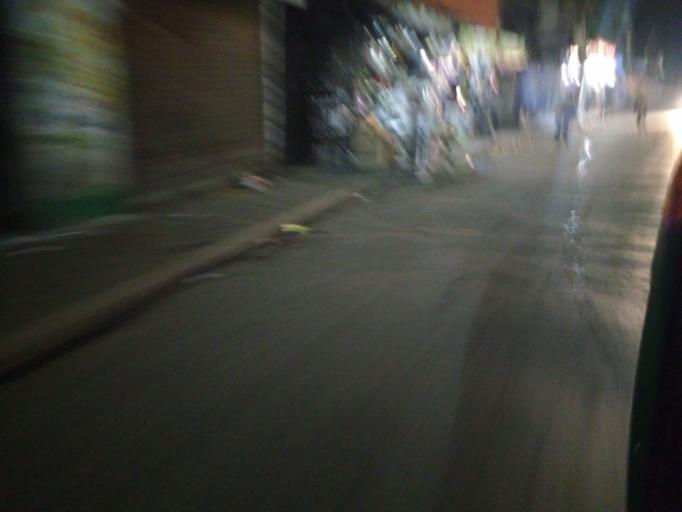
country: IN
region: West Bengal
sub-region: North 24 Parganas
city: Baranagar
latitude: 22.6324
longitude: 88.3725
